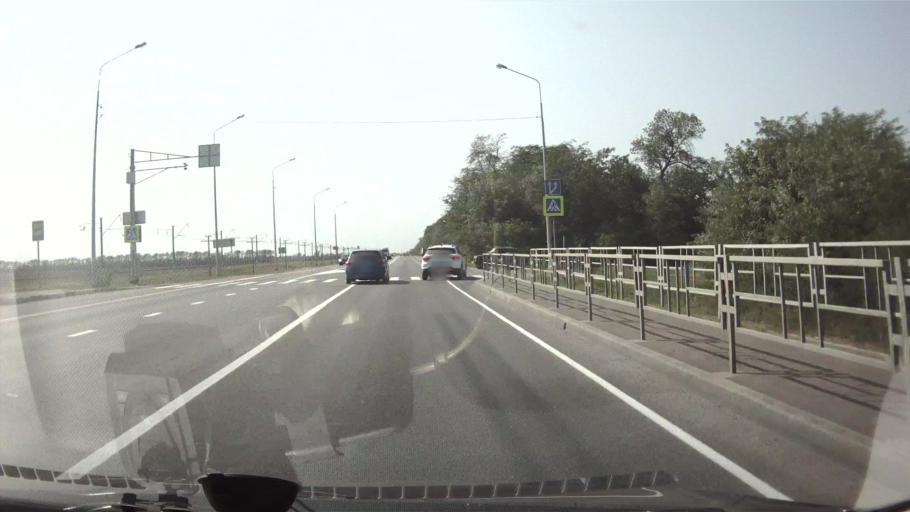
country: RU
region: Krasnodarskiy
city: Ladozhskaya
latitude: 45.3023
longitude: 39.8961
